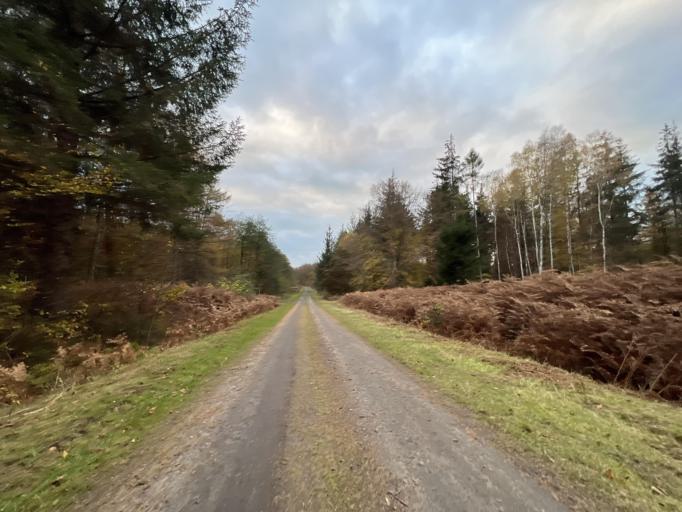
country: DE
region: Mecklenburg-Vorpommern
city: Putbus
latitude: 54.3678
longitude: 13.4493
